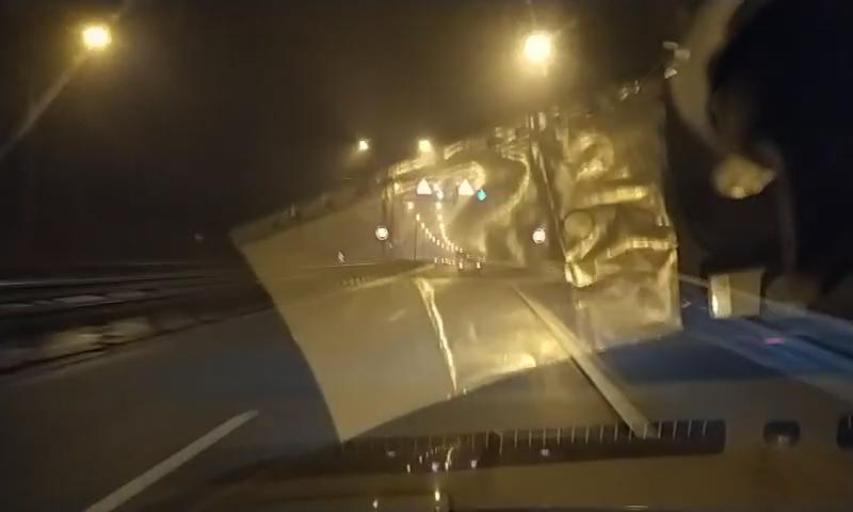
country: RU
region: Leningrad
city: Bugry
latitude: 60.1173
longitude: 30.3864
